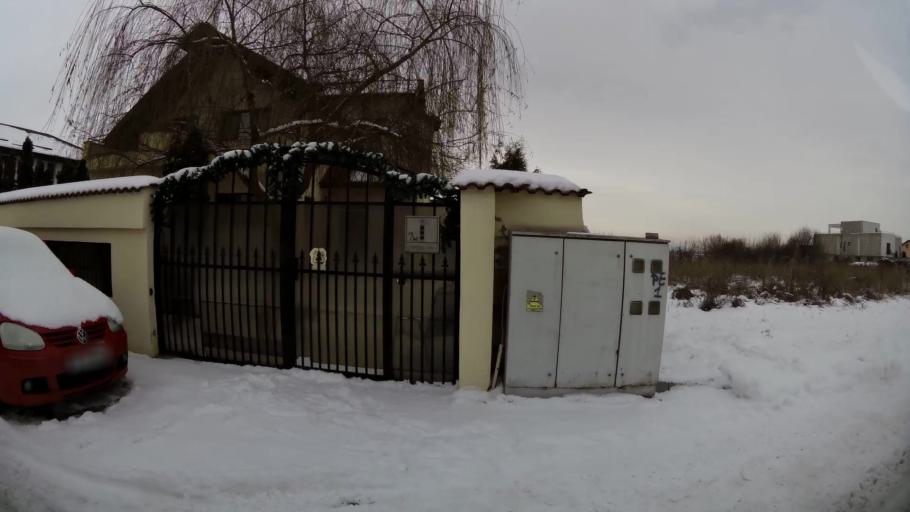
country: RO
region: Ilfov
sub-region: Voluntari City
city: Voluntari
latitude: 44.5114
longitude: 26.1424
